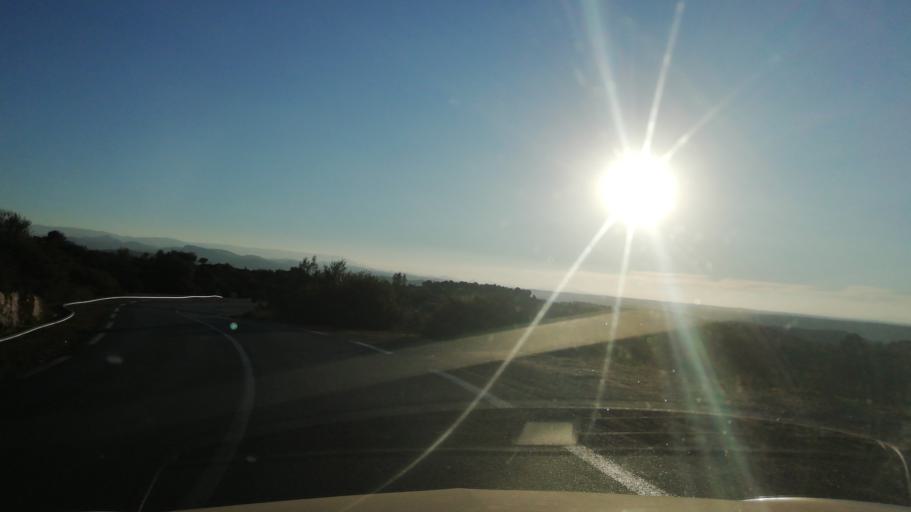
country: DZ
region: Tlemcen
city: Beni Mester
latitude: 34.8153
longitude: -1.6195
